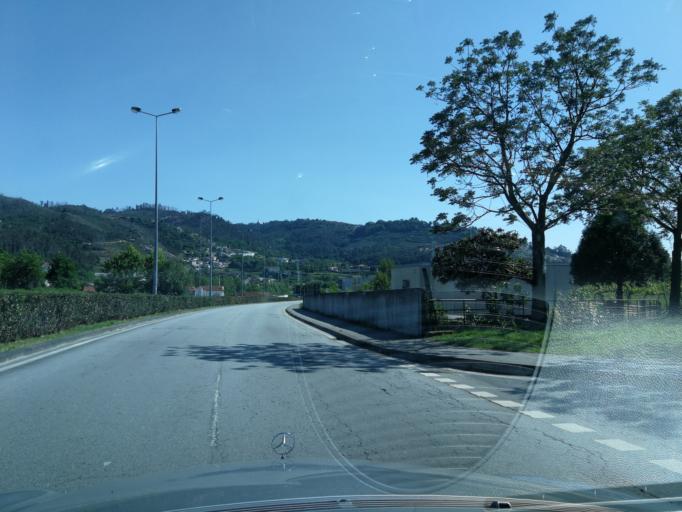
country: PT
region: Braga
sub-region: Braga
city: Adaufe
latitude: 41.5727
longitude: -8.3688
